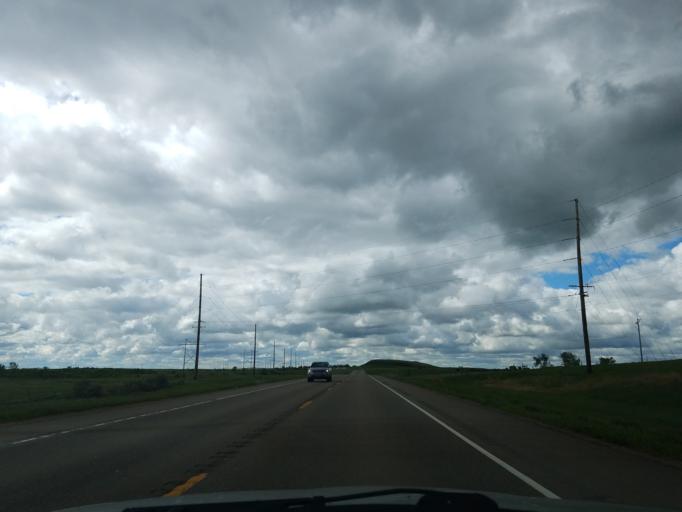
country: US
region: North Dakota
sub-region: McKenzie County
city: Watford City
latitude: 47.4091
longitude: -103.2480
